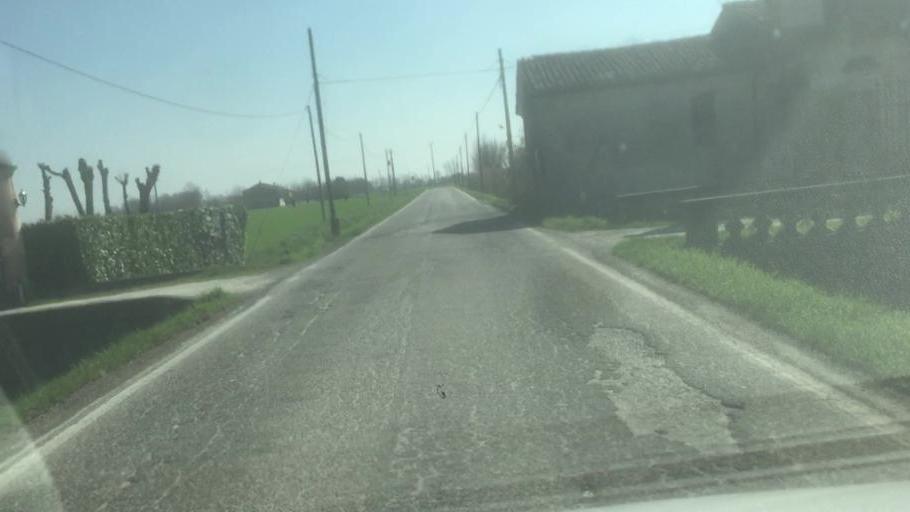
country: IT
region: Lombardy
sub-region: Provincia di Mantova
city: Medole
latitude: 45.2870
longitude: 10.5304
